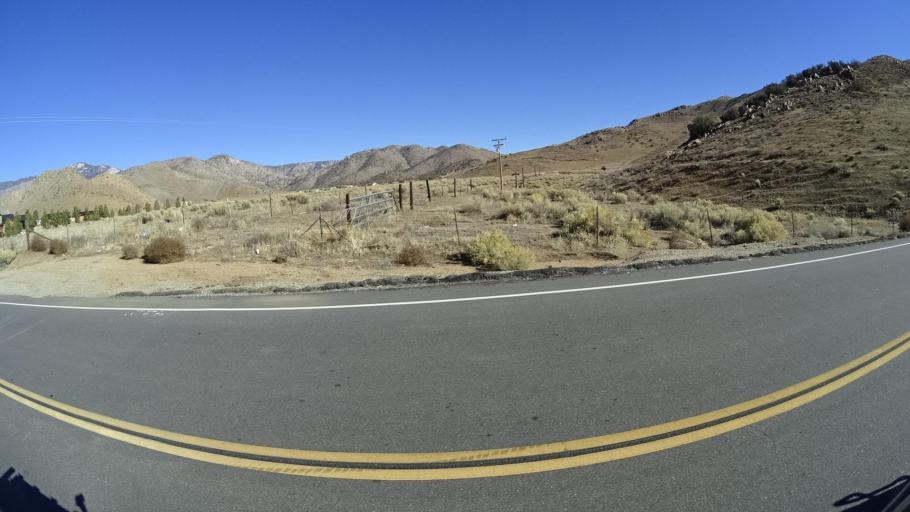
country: US
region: California
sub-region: Kern County
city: Wofford Heights
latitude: 35.7027
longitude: -118.4233
